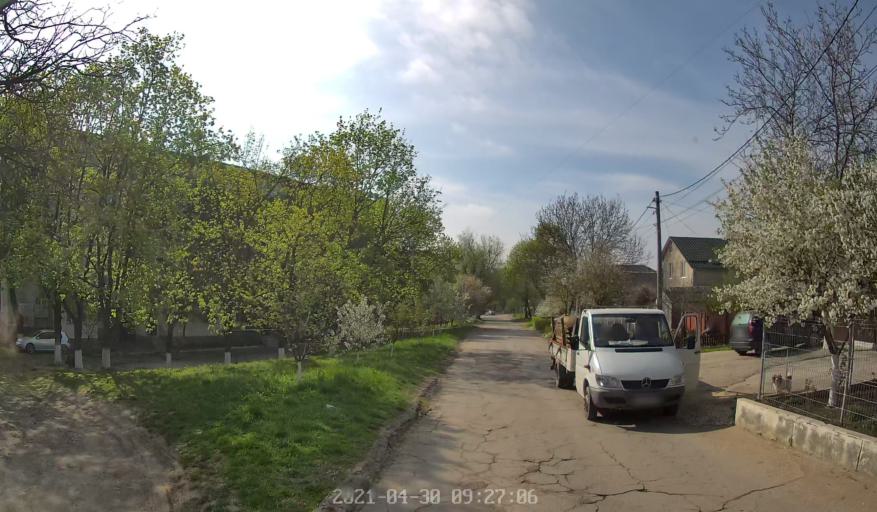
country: MD
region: Chisinau
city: Chisinau
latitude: 47.0268
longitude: 28.8814
